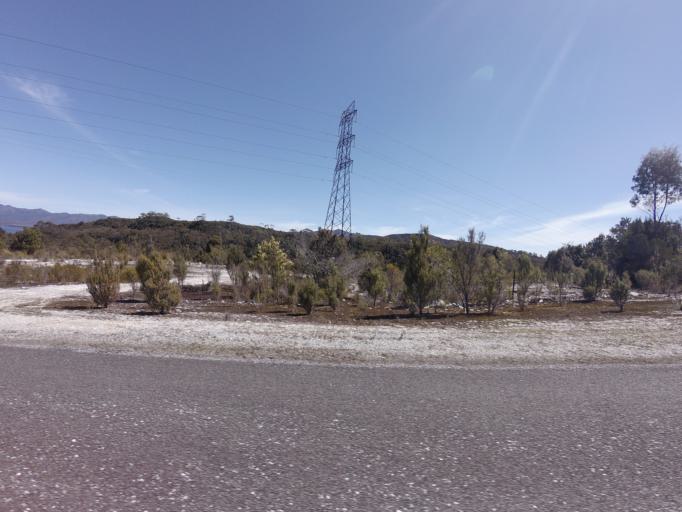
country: AU
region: Tasmania
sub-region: West Coast
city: Queenstown
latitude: -42.7695
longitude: 146.0566
